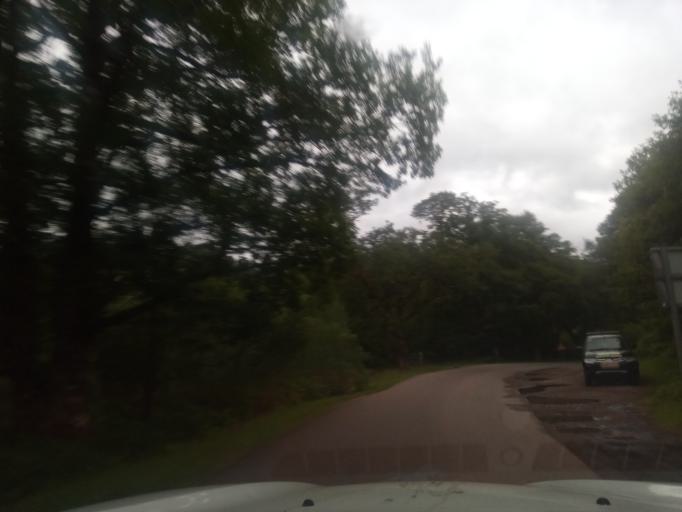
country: GB
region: Scotland
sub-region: Highland
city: Fort William
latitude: 56.8600
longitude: -5.3489
